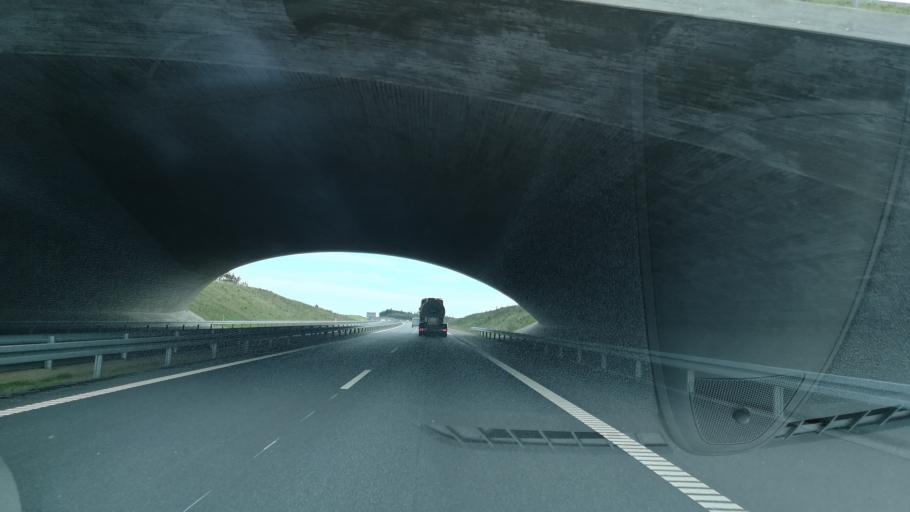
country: DK
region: Central Jutland
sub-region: Herning Kommune
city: Avlum
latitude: 56.2792
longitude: 8.7402
